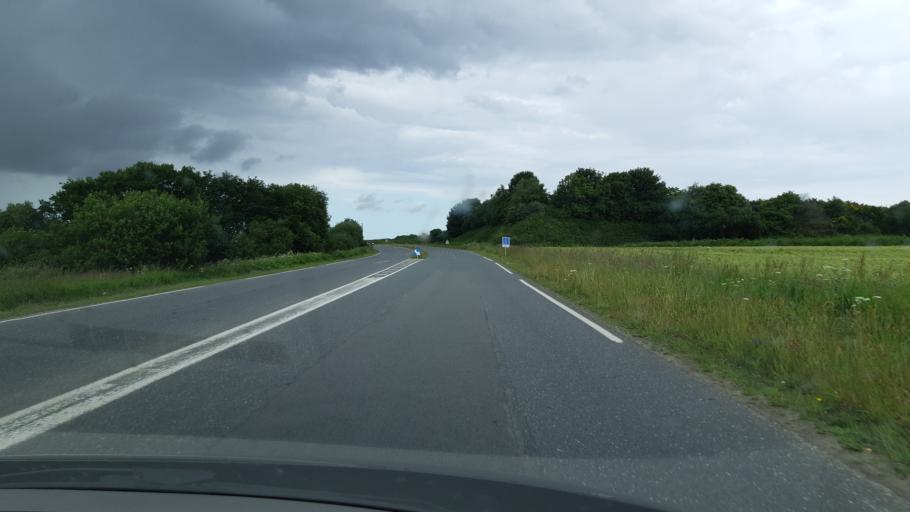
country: FR
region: Brittany
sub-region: Departement du Finistere
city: Plouvorn
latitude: 48.5993
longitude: -4.0524
